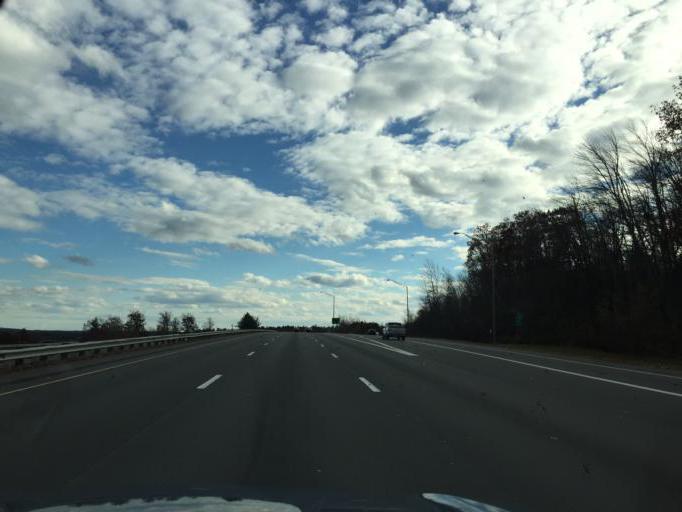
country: US
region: New Hampshire
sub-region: Hillsborough County
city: Hudson
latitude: 42.7293
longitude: -71.4524
